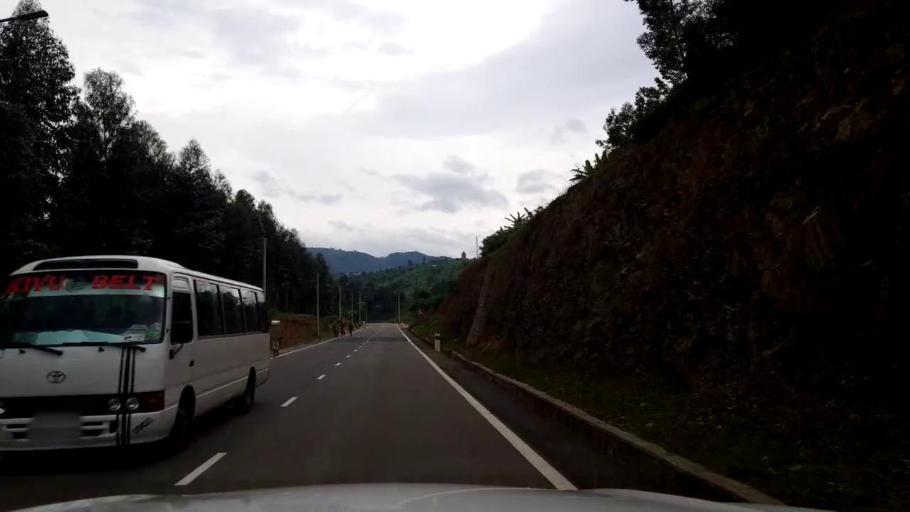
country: RW
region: Western Province
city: Kibuye
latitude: -2.0210
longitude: 29.3891
